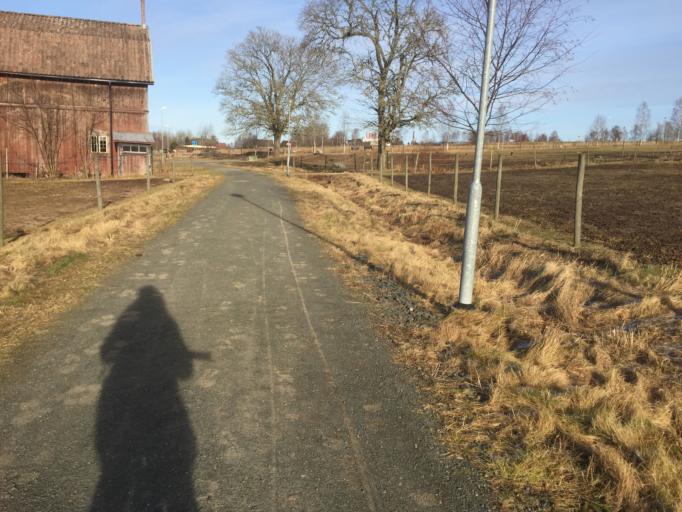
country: SE
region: Joenkoeping
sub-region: Aneby Kommun
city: Aneby
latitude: 57.8255
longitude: 14.8155
